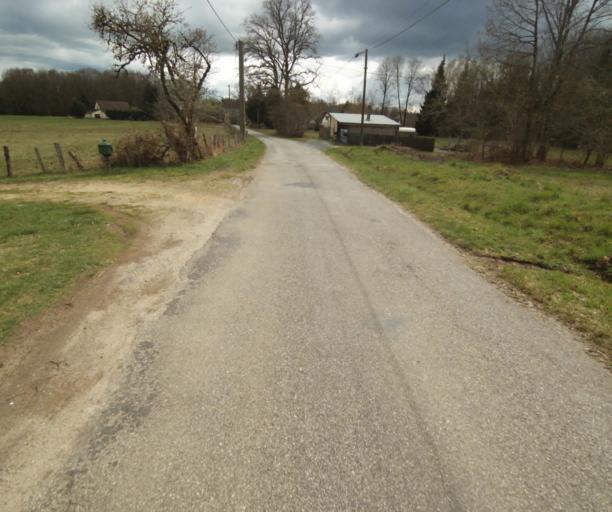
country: FR
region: Limousin
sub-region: Departement de la Correze
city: Correze
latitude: 45.2763
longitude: 1.9797
